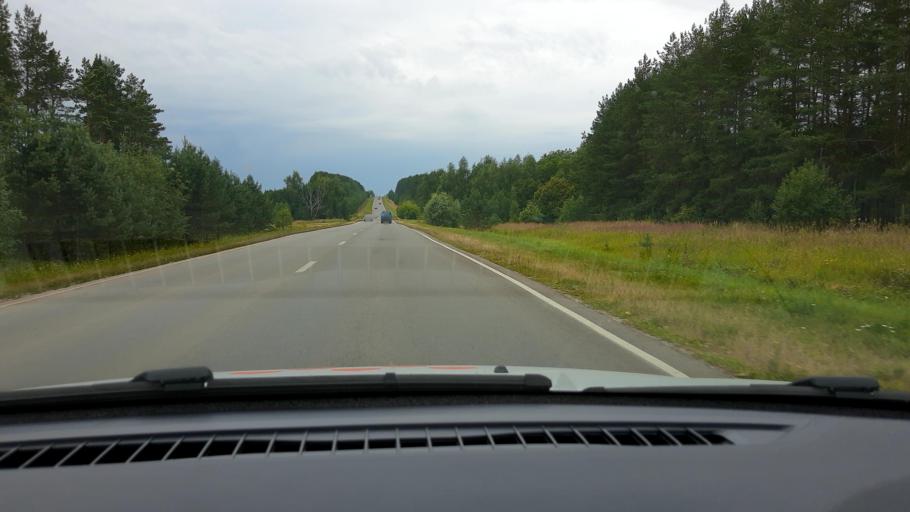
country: RU
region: Nizjnij Novgorod
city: Vyyezdnoye
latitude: 55.1629
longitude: 43.5851
